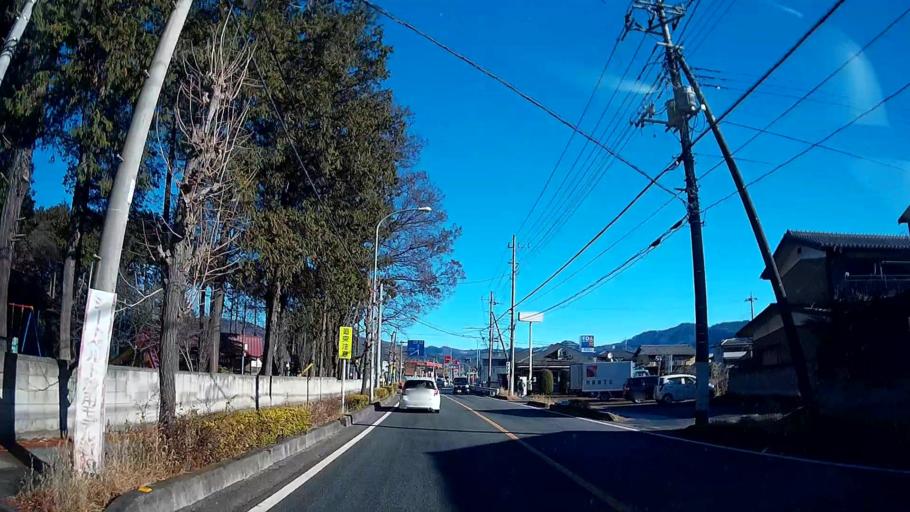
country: JP
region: Saitama
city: Chichibu
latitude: 36.0194
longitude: 139.0957
